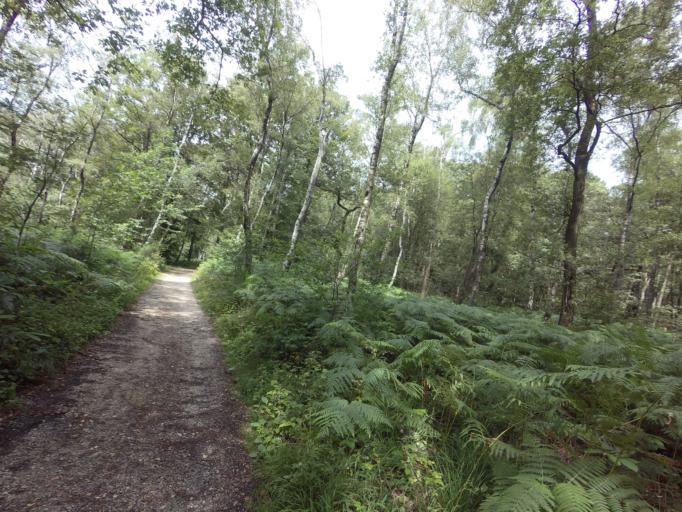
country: BE
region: Wallonia
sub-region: Province de Liege
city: Plombieres
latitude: 50.7594
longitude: 5.9743
